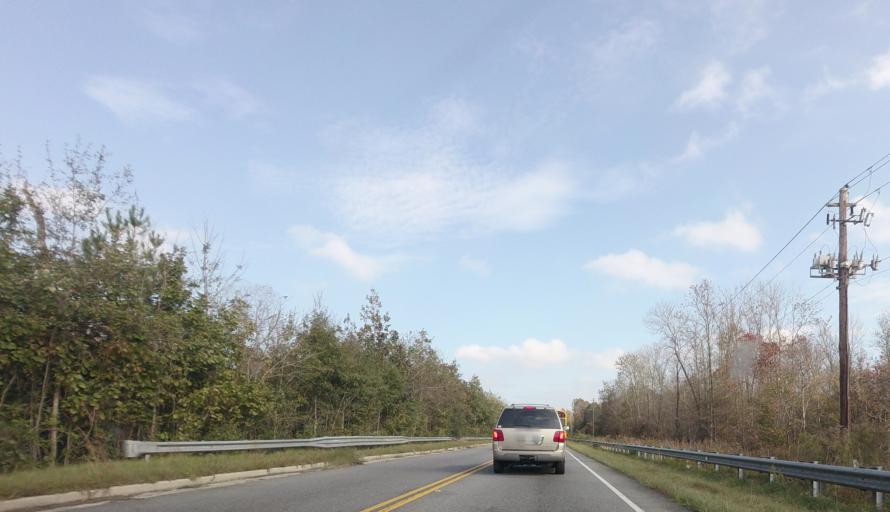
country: US
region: Georgia
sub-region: Bibb County
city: Macon
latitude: 32.8060
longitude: -83.6818
